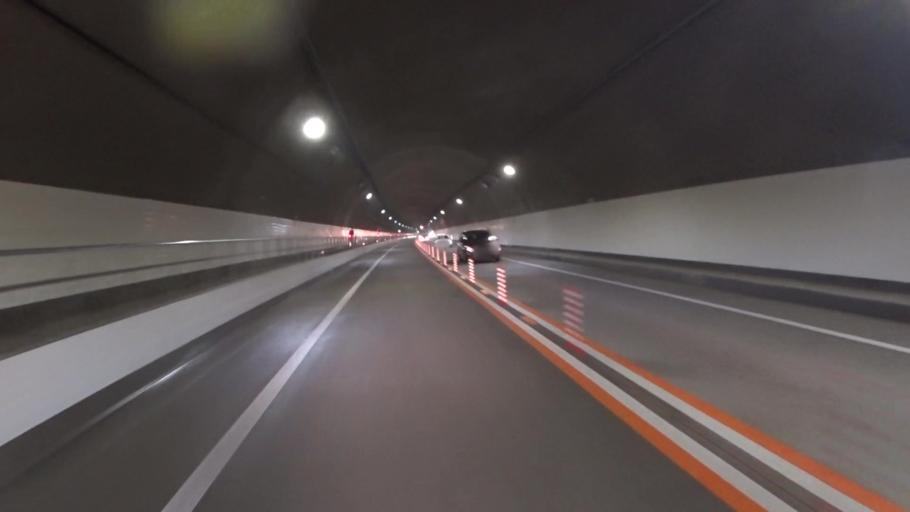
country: JP
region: Kyoto
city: Ayabe
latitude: 35.2421
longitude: 135.3433
